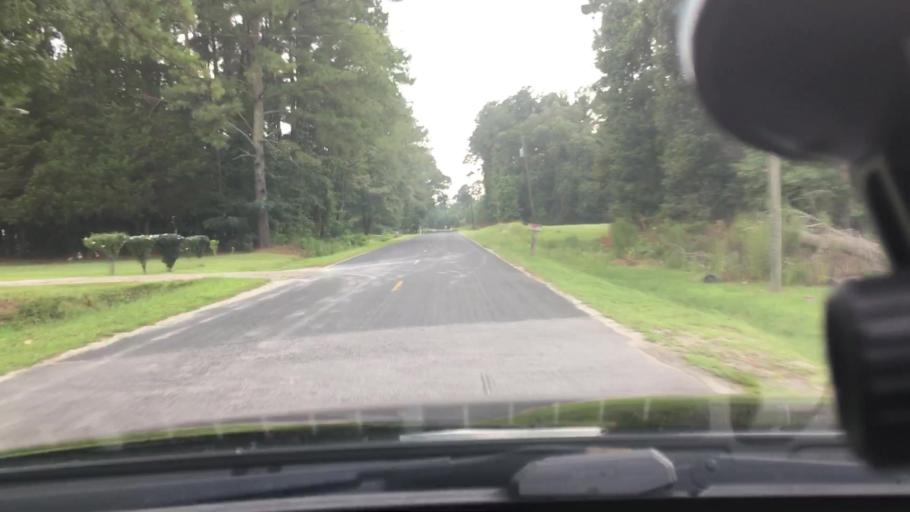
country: US
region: North Carolina
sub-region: Craven County
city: Vanceboro
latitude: 35.3348
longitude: -77.1657
